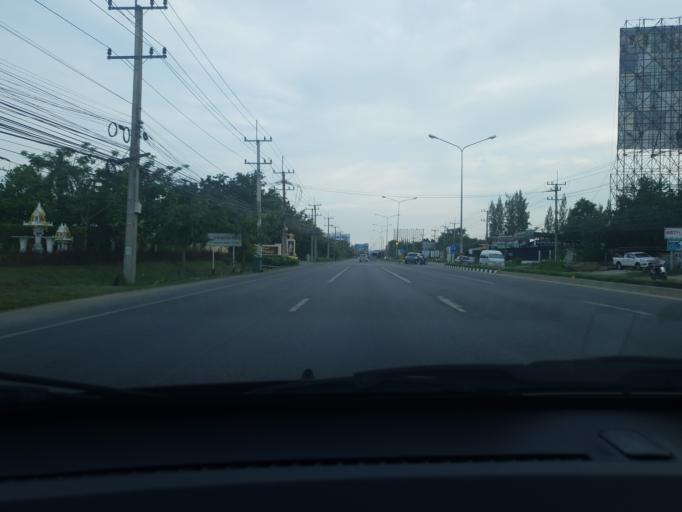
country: TH
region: Prachuap Khiri Khan
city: Hua Hin
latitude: 12.6595
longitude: 99.9522
